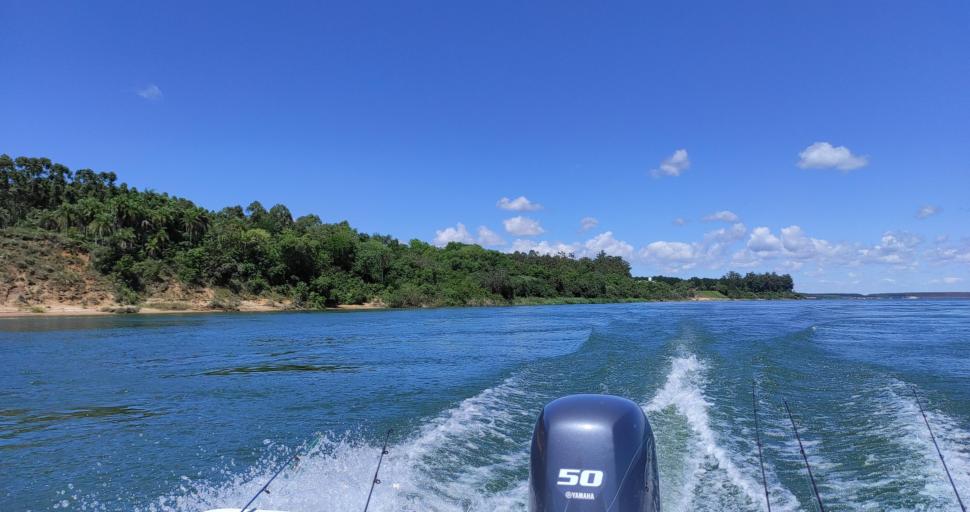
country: AR
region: Corrientes
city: Ituzaingo
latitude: -27.5898
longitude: -56.7974
